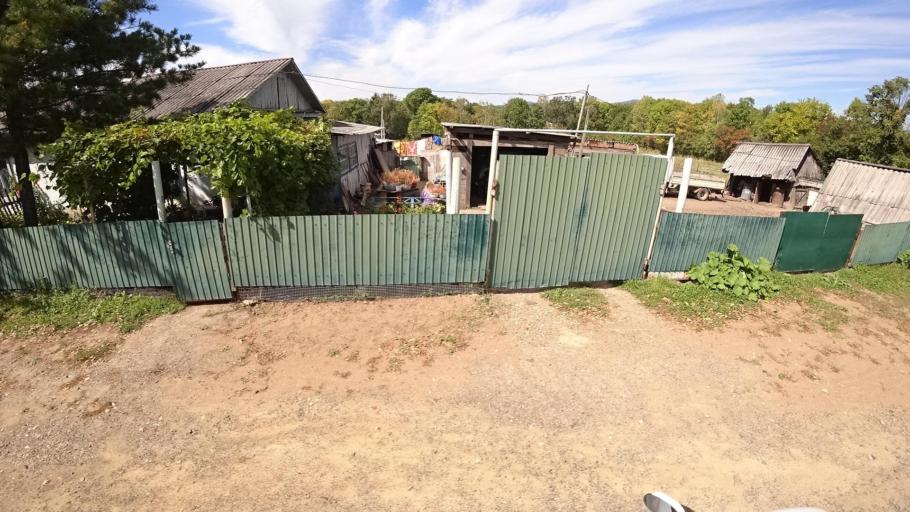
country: RU
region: Primorskiy
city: Yakovlevka
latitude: 44.7064
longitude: 133.6418
